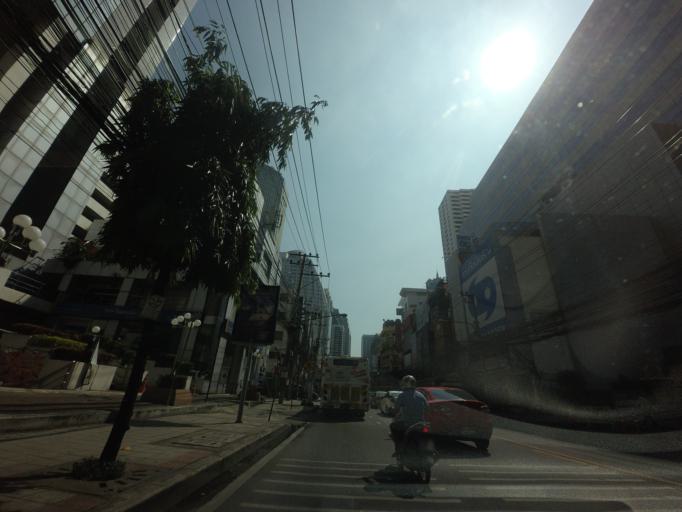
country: TH
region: Bangkok
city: Watthana
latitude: 13.7412
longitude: 100.5620
